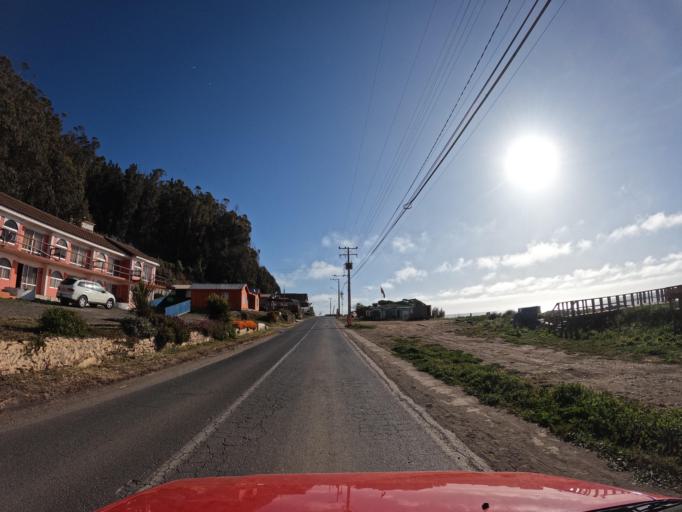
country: CL
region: Maule
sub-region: Provincia de Talca
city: Constitucion
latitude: -34.8894
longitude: -72.1726
